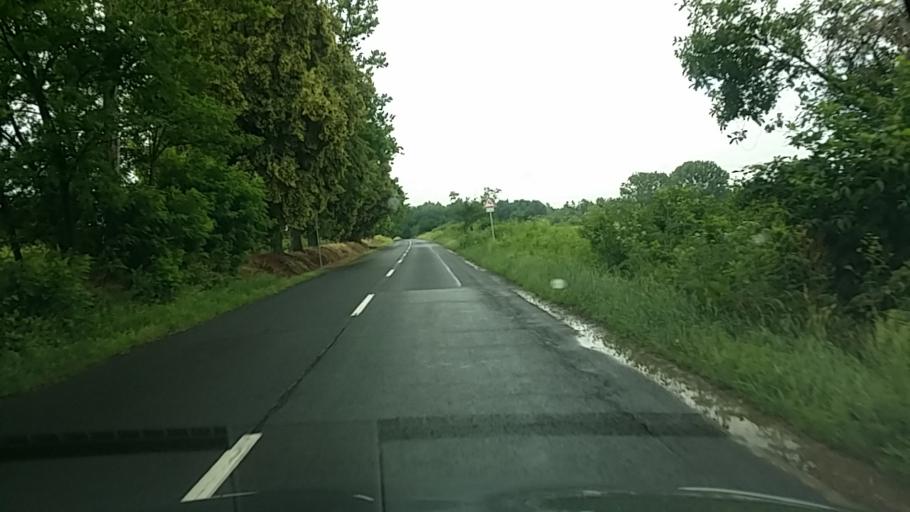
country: SK
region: Nitriansky
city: Sahy
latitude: 48.0513
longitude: 18.9241
